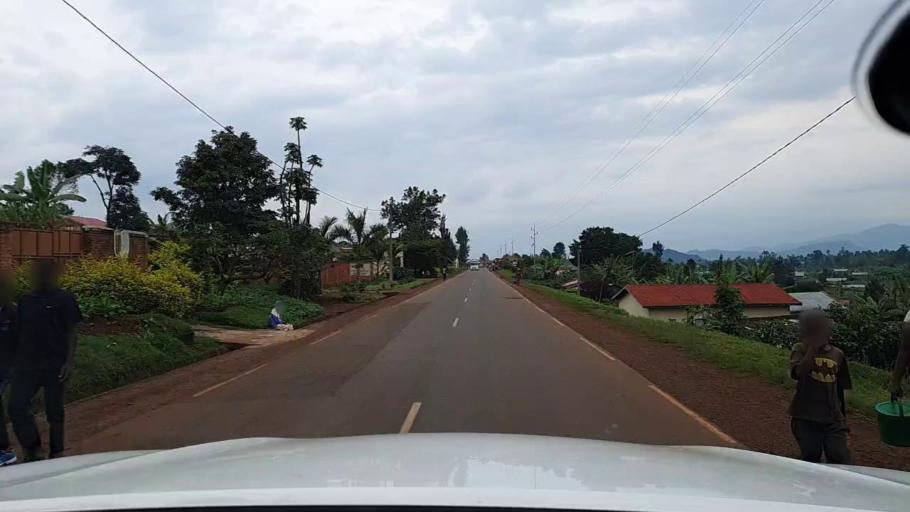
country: RW
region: Western Province
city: Cyangugu
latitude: -2.6409
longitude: 28.9530
